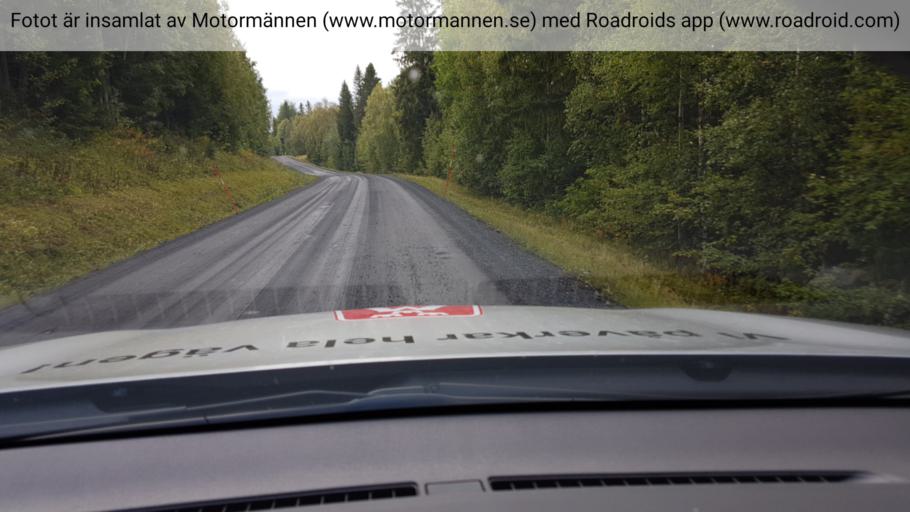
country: SE
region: Jaemtland
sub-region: Stroemsunds Kommun
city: Stroemsund
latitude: 64.1432
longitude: 15.7051
